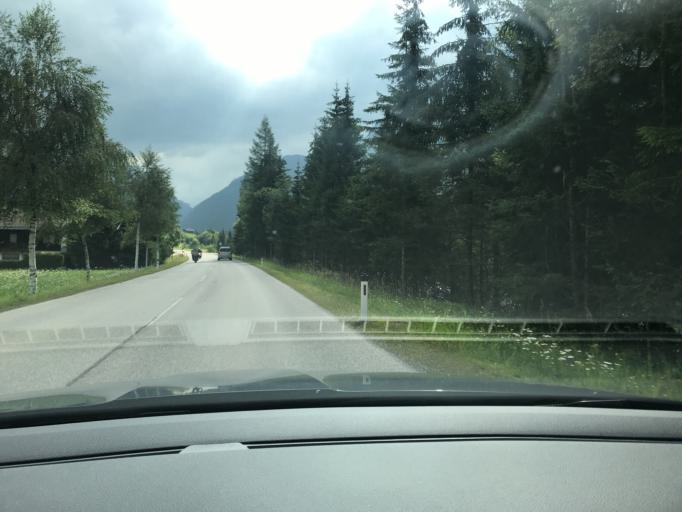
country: AT
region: Tyrol
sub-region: Politischer Bezirk Lienz
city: Virgen
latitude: 46.9171
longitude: 12.3962
